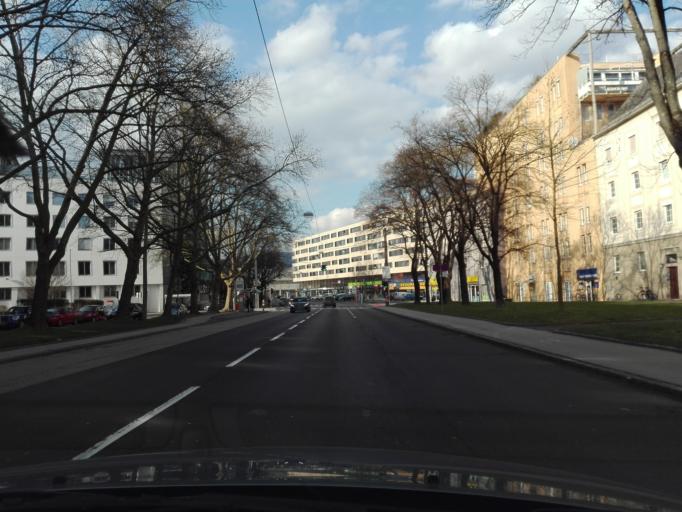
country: AT
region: Upper Austria
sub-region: Linz Stadt
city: Linz
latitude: 48.3087
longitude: 14.2994
